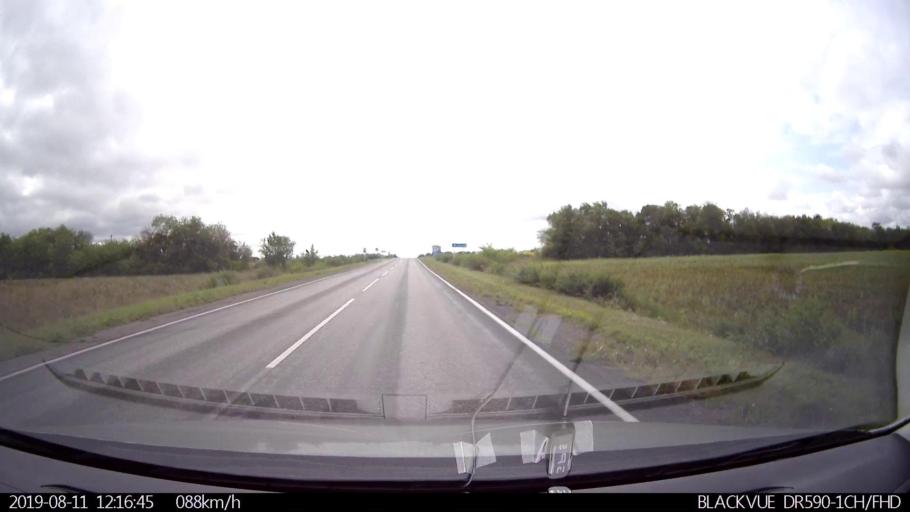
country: RU
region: Ulyanovsk
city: Ignatovka
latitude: 53.9252
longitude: 47.9591
